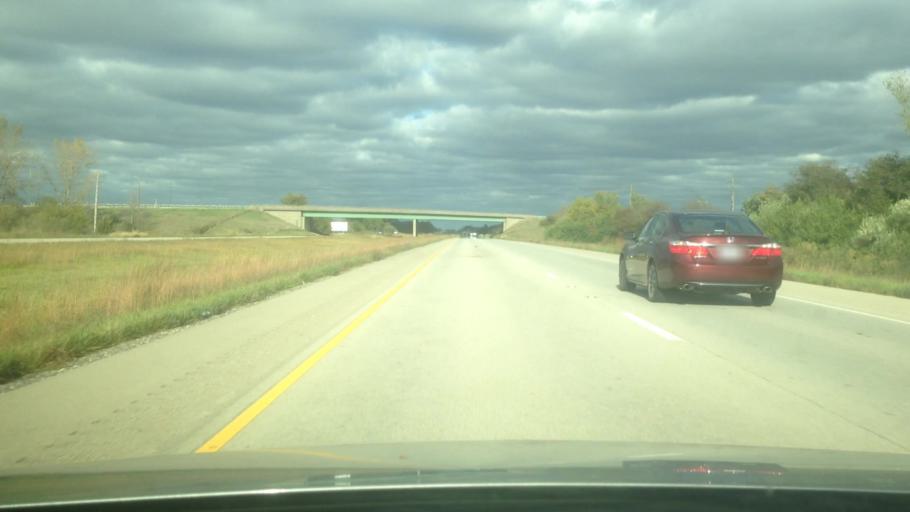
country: US
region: Illinois
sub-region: Macon County
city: Forsyth
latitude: 39.9175
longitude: -88.8623
